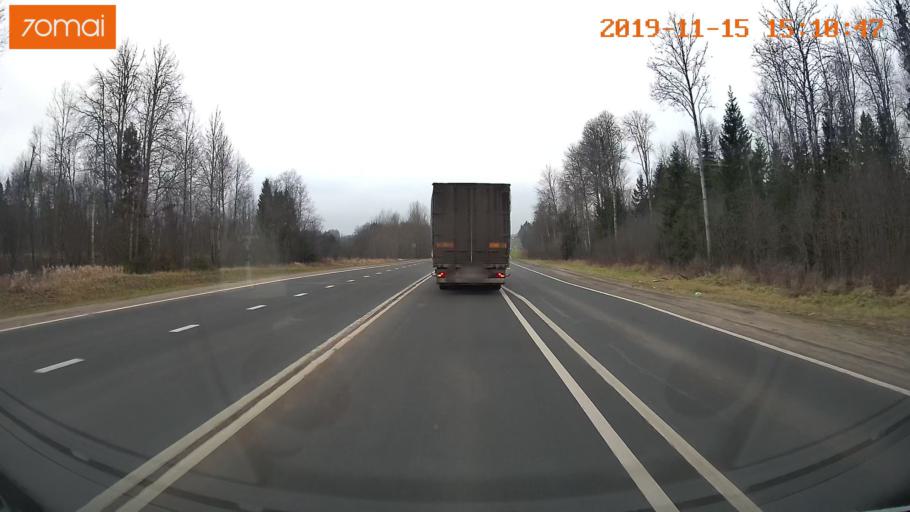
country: RU
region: Jaroslavl
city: Prechistoye
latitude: 58.3442
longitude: 40.2507
